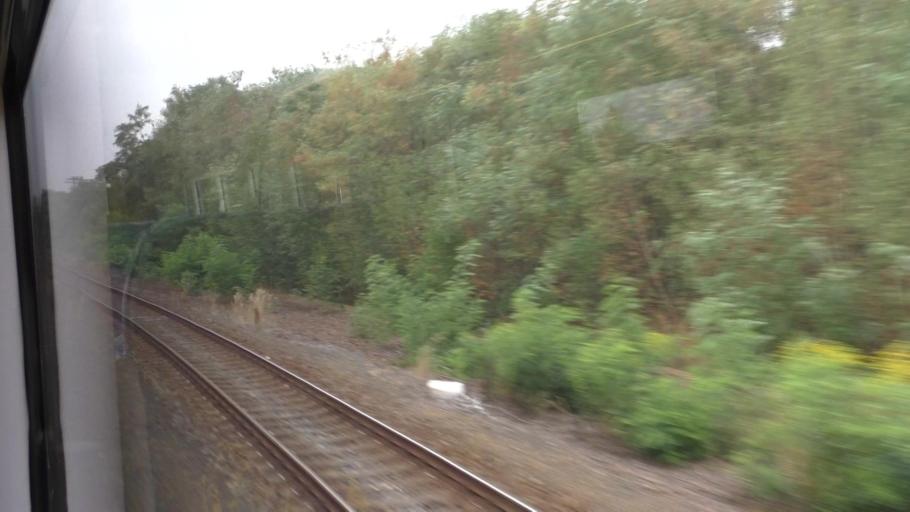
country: DE
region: Saxony
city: Ostritz
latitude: 51.0724
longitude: 14.9615
